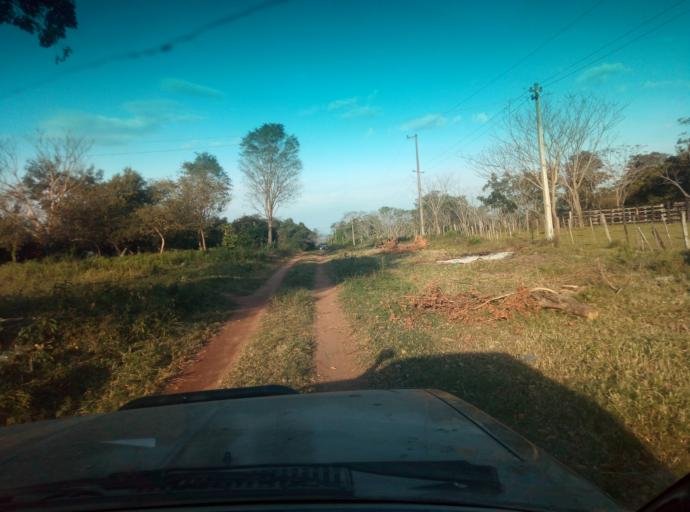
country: PY
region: Caaguazu
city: Doctor Cecilio Baez
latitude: -25.1517
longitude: -56.2501
